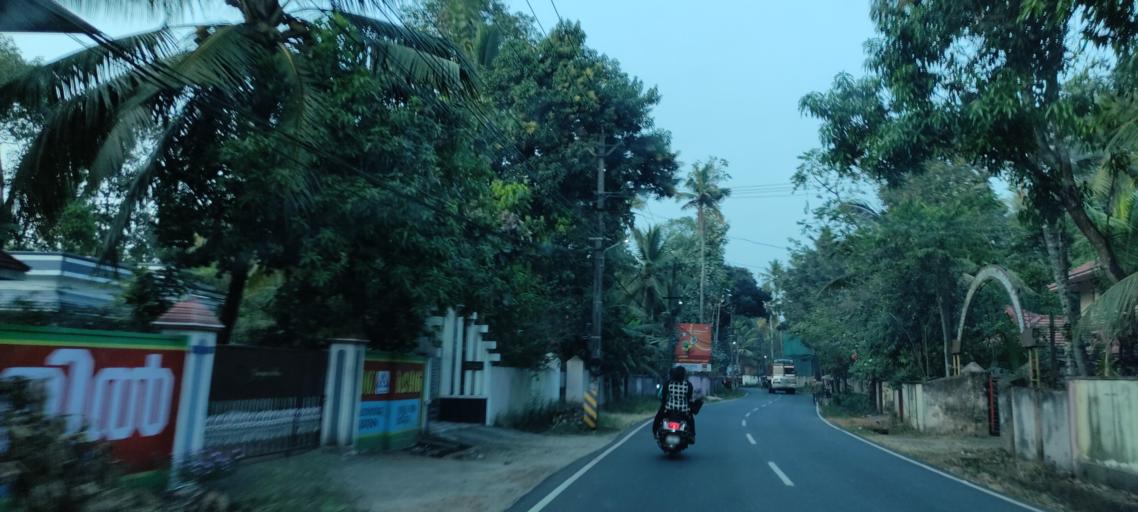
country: IN
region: Kerala
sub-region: Alappuzha
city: Mavelikara
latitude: 9.2695
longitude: 76.5380
